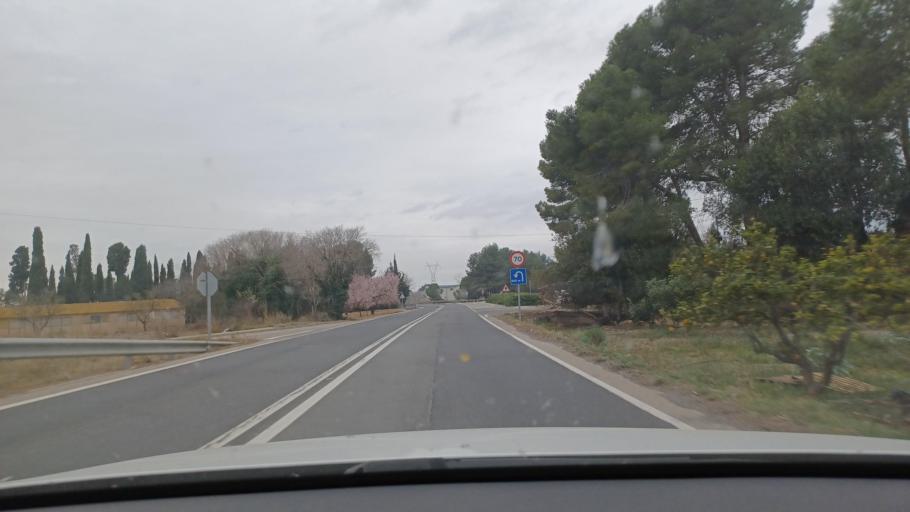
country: ES
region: Catalonia
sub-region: Provincia de Tarragona
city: Santa Barbara
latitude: 40.6828
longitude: 0.4608
